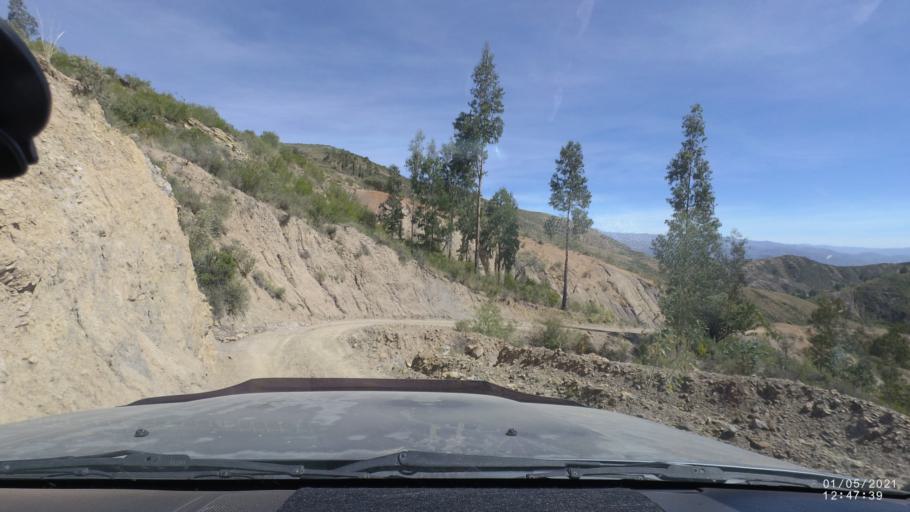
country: BO
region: Cochabamba
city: Capinota
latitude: -17.6868
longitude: -66.1613
